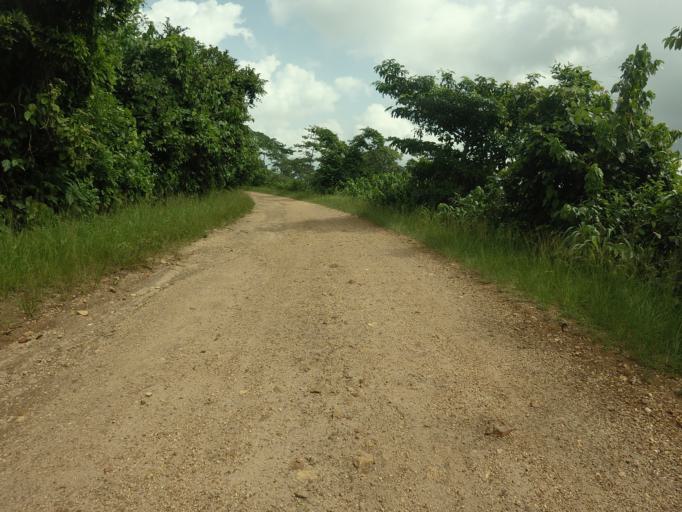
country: GH
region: Volta
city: Kpandu
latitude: 6.8446
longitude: 0.4318
